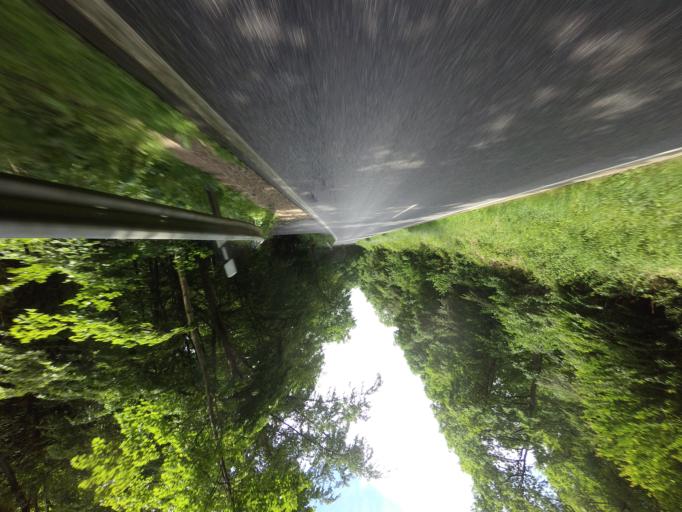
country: DE
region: Rheinland-Pfalz
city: Herschbroich
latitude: 50.3860
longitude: 6.9740
